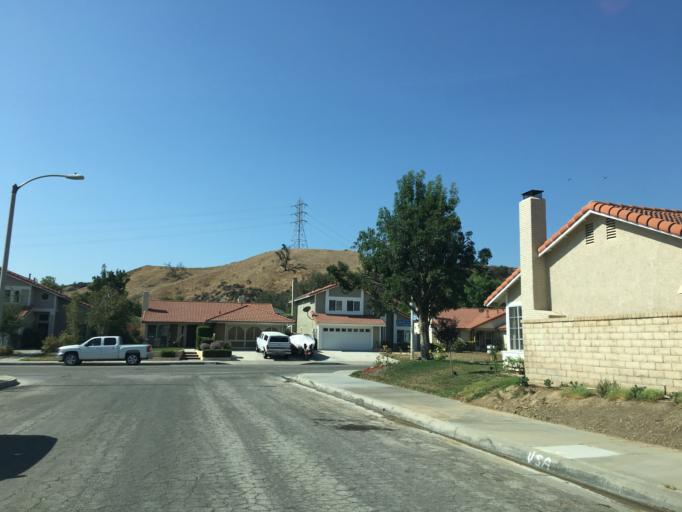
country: US
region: California
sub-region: Los Angeles County
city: Valencia
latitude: 34.4494
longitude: -118.6219
